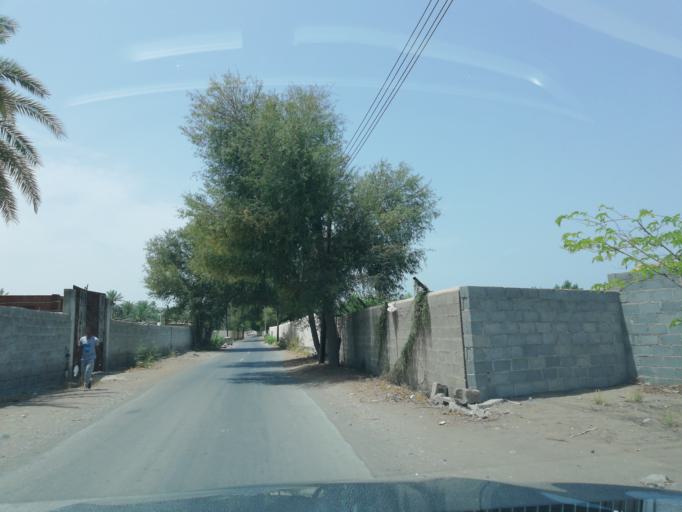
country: OM
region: Muhafazat Masqat
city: As Sib al Jadidah
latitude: 23.6616
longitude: 58.2078
